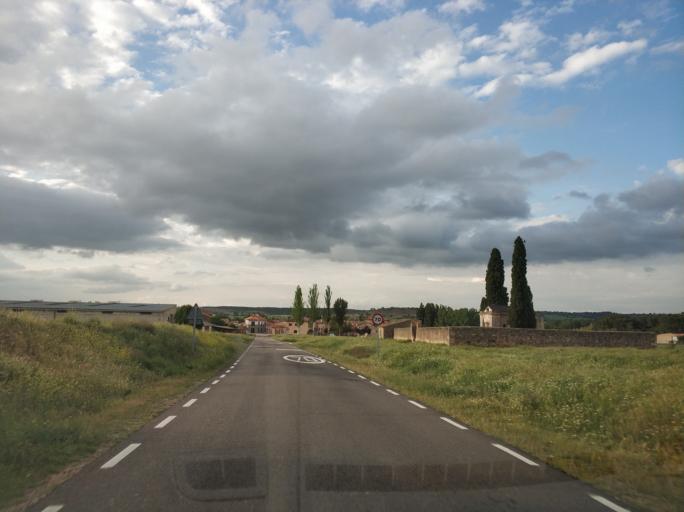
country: ES
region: Castille and Leon
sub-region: Provincia de Burgos
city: San Juan del Monte
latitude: 41.6789
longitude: -3.5242
